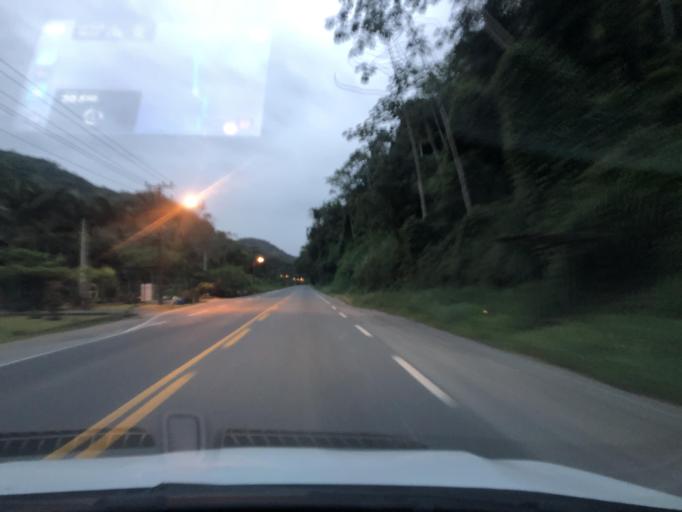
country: BR
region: Santa Catarina
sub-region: Pomerode
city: Pomerode
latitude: -26.7120
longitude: -49.0562
